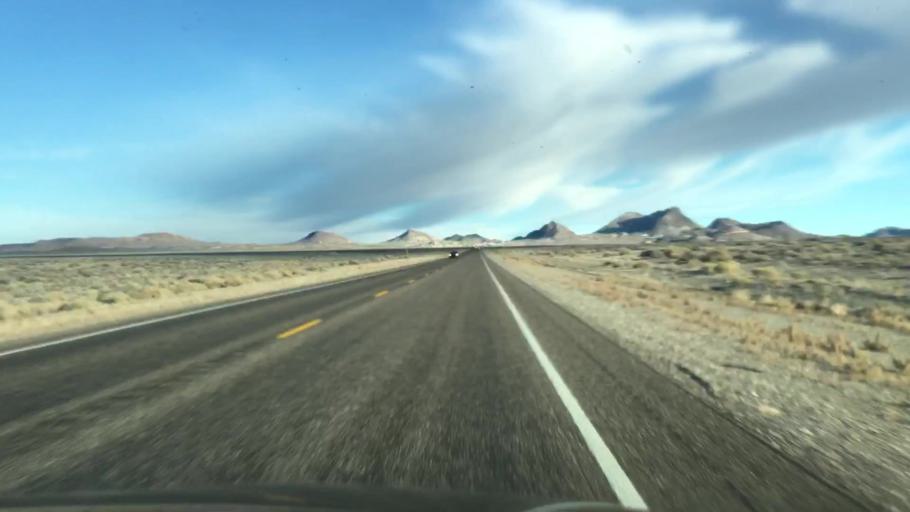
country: US
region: Nevada
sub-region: Nye County
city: Tonopah
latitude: 38.0979
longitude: -117.3217
